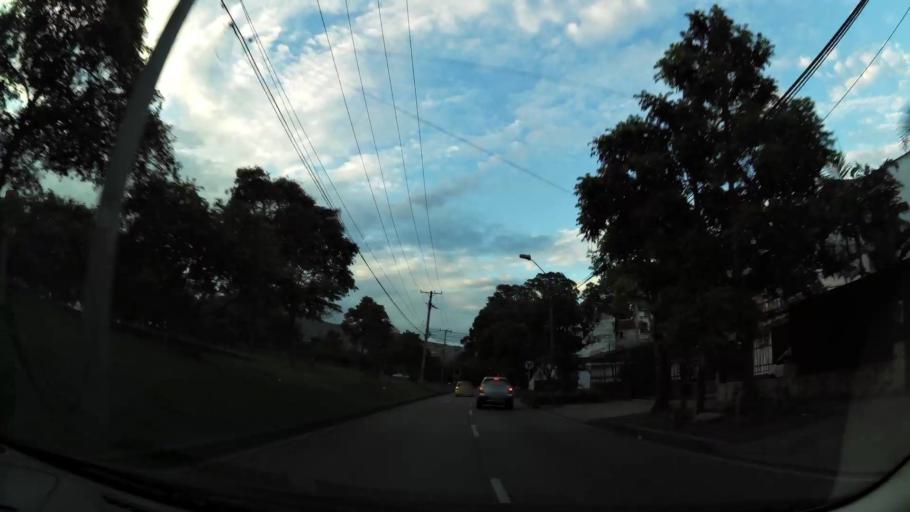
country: CO
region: Valle del Cauca
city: Cali
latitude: 3.4707
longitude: -76.5236
